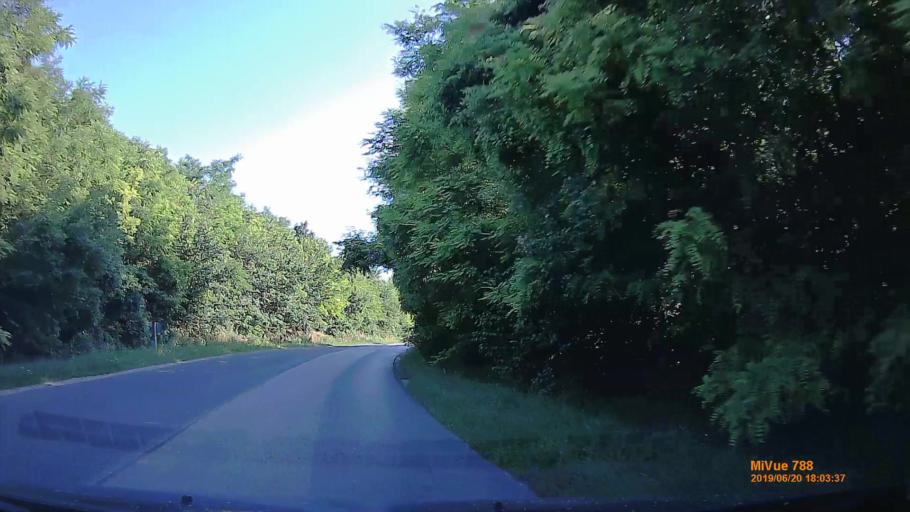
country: HU
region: Baranya
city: Szentlorinc
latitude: 46.0591
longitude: 17.9908
